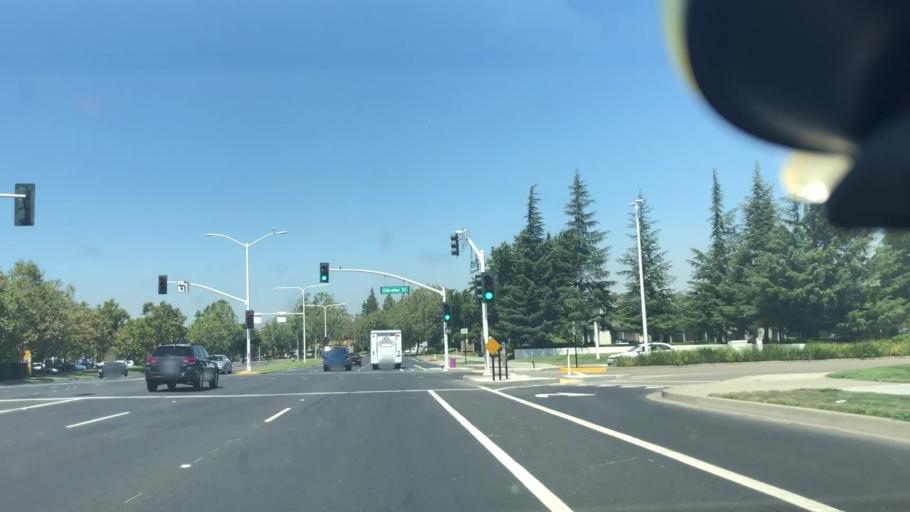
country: US
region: California
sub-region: Alameda County
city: Dublin
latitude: 37.6956
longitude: -121.9035
